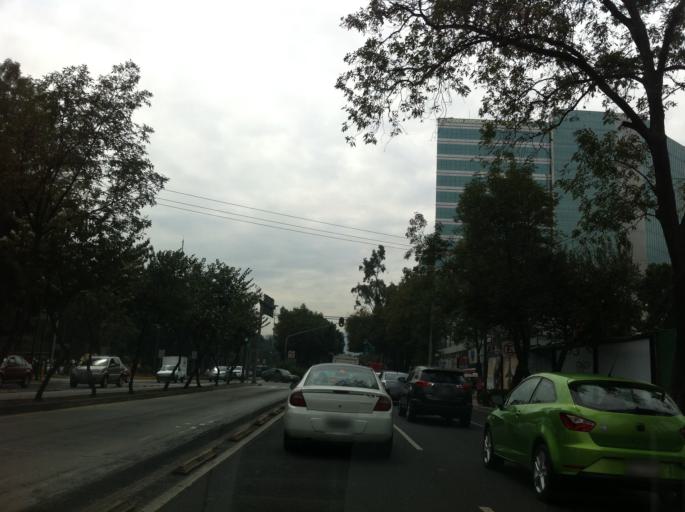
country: MX
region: Mexico City
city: Alvaro Obregon
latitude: 19.3497
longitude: -99.1868
